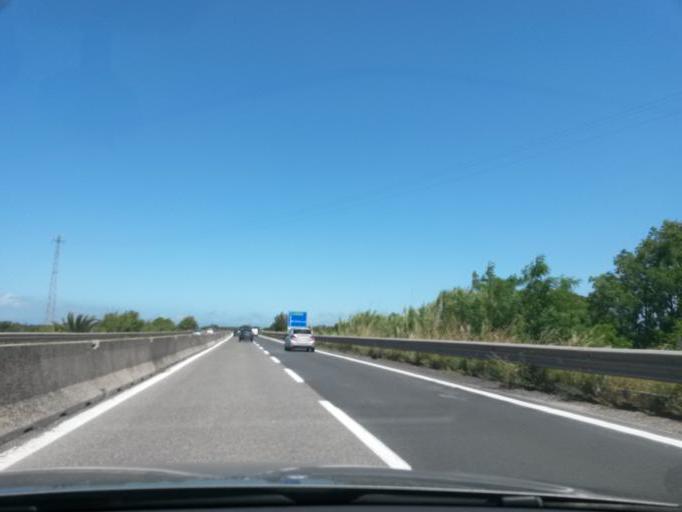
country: IT
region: Tuscany
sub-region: Provincia di Livorno
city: S.P. in Palazzi
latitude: 43.3254
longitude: 10.5297
